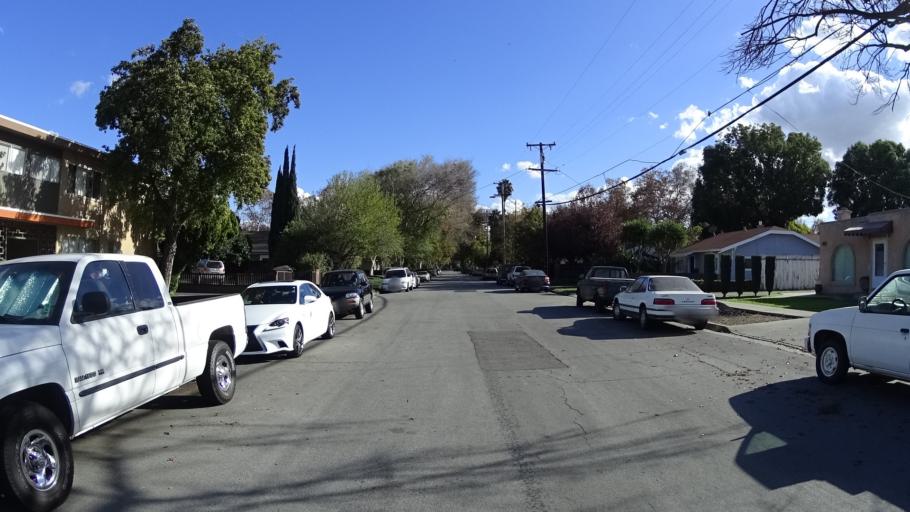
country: US
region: California
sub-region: Santa Clara County
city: Burbank
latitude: 37.3444
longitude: -121.9220
